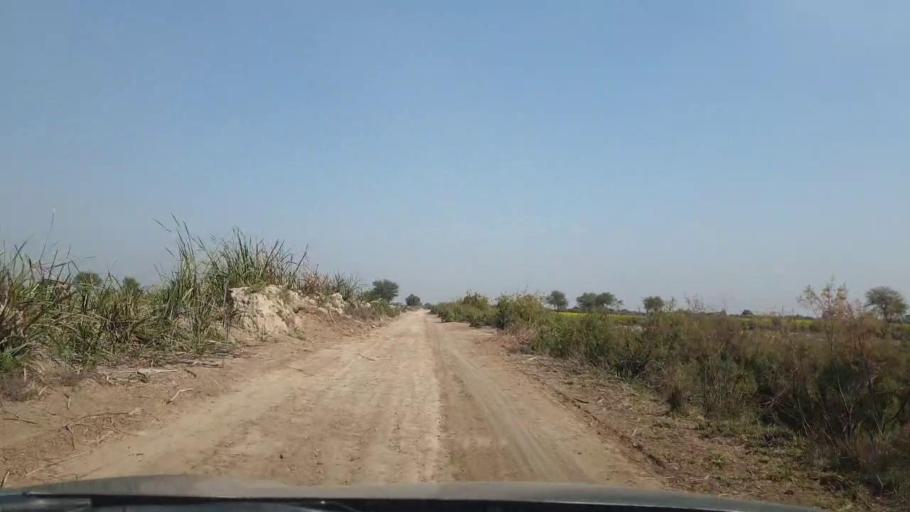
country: PK
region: Sindh
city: Berani
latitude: 25.6590
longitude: 68.8836
